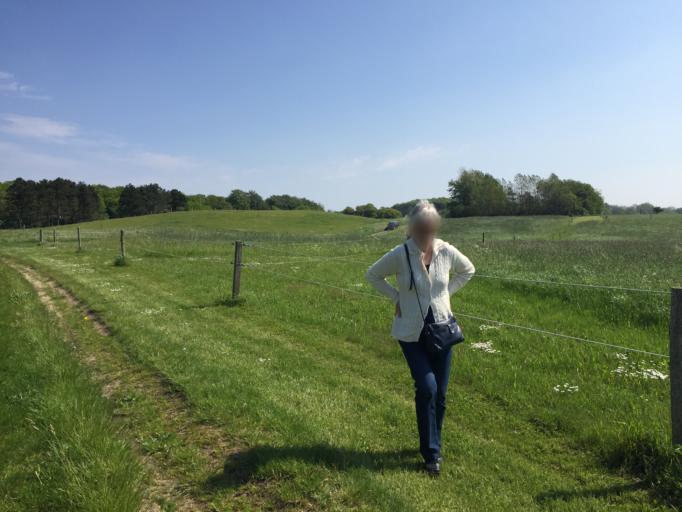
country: DK
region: South Denmark
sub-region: Langeland Kommune
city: Rudkobing
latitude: 55.0144
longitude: 10.8258
